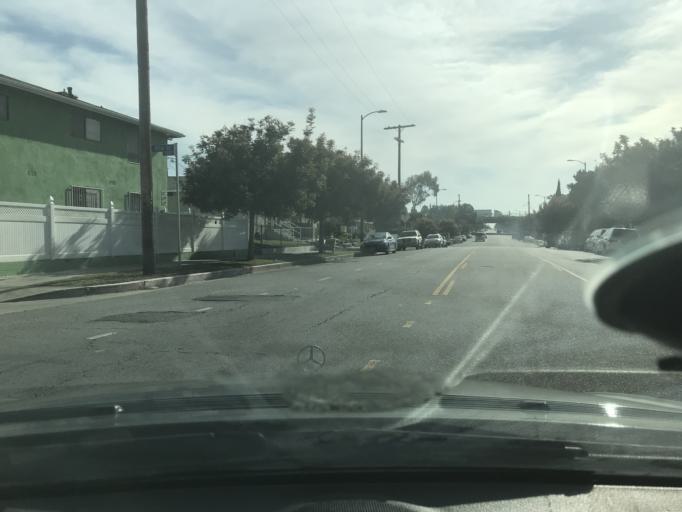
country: US
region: California
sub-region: Los Angeles County
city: Willowbrook
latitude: 33.9301
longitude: -118.2695
